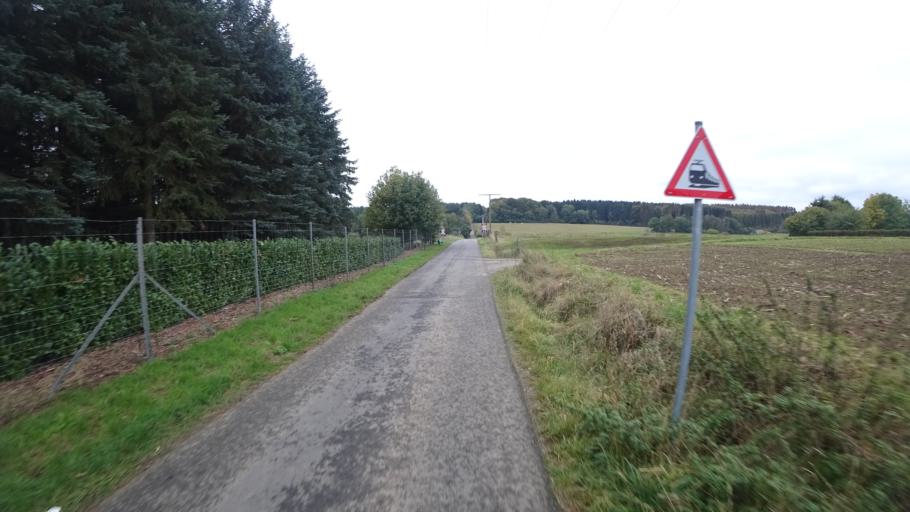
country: DE
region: Rheinland-Pfalz
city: Marienrachdorf
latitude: 50.5462
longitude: 7.7101
